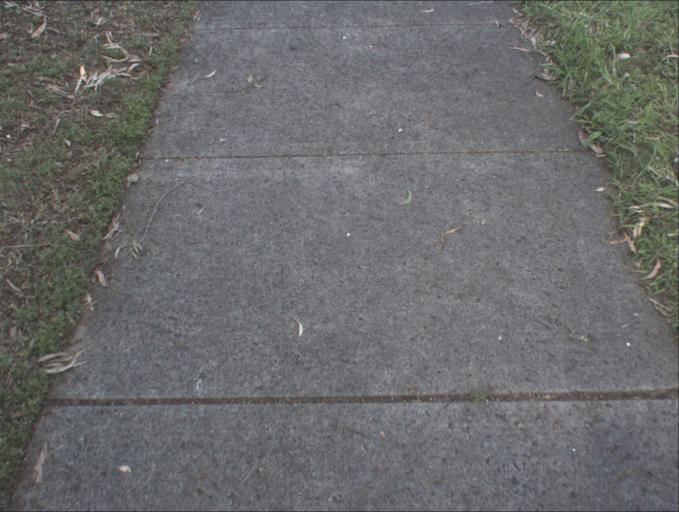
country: AU
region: Queensland
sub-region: Logan
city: Cedar Vale
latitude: -27.8313
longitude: 153.0268
